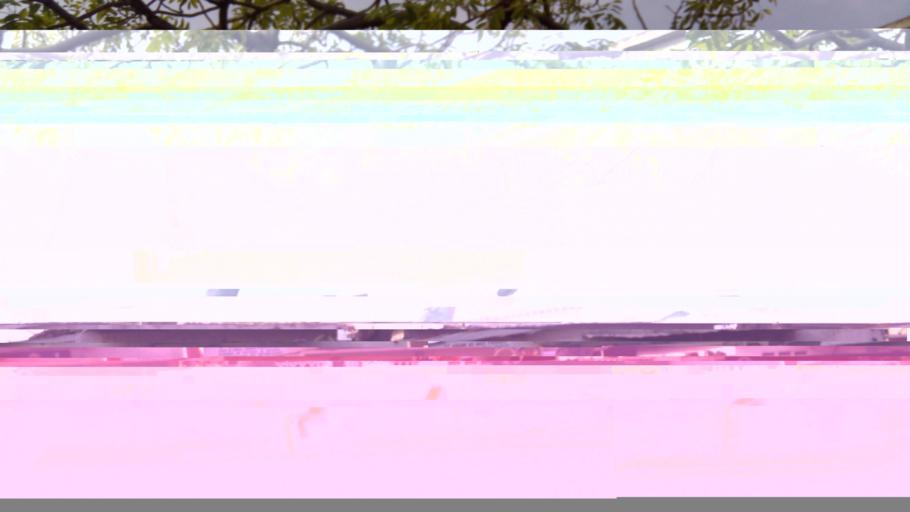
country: BJ
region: Littoral
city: Cotonou
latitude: 6.3704
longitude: 2.4226
